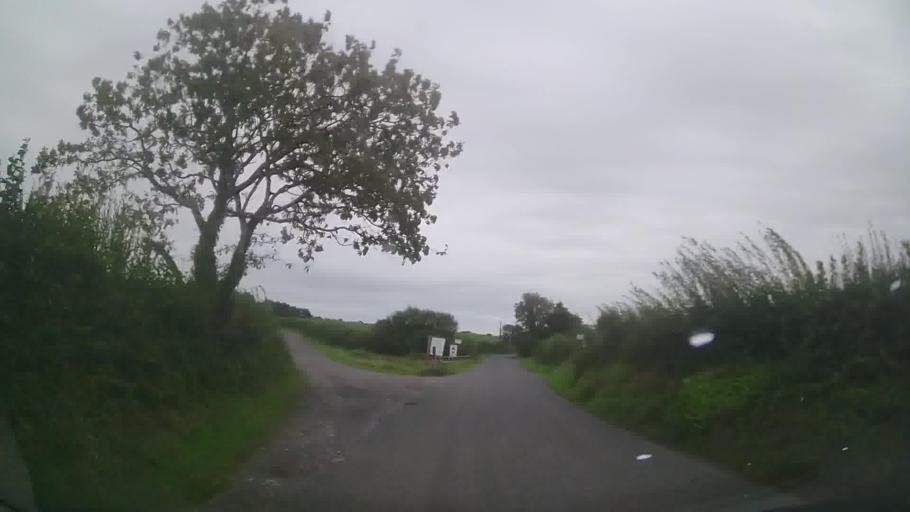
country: GB
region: Wales
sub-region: Carmarthenshire
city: Whitland
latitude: 51.7472
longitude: -4.6168
